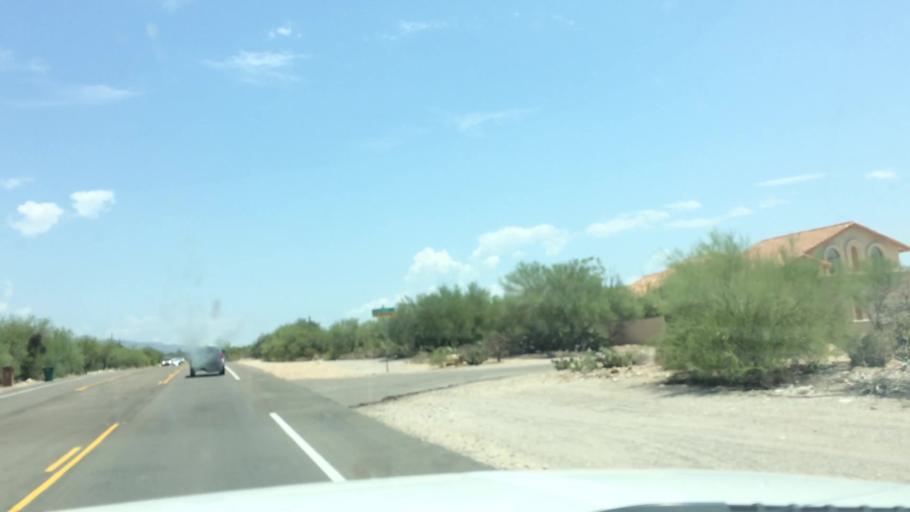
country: US
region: Arizona
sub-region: Pima County
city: Casas Adobes
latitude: 32.3227
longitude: -110.9566
